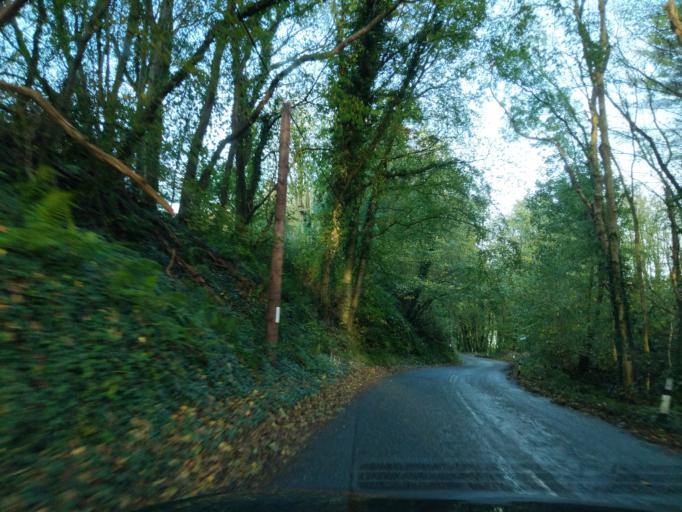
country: GB
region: Scotland
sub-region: Dumfries and Galloway
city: Kirkcudbright
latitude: 54.8129
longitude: -4.0948
